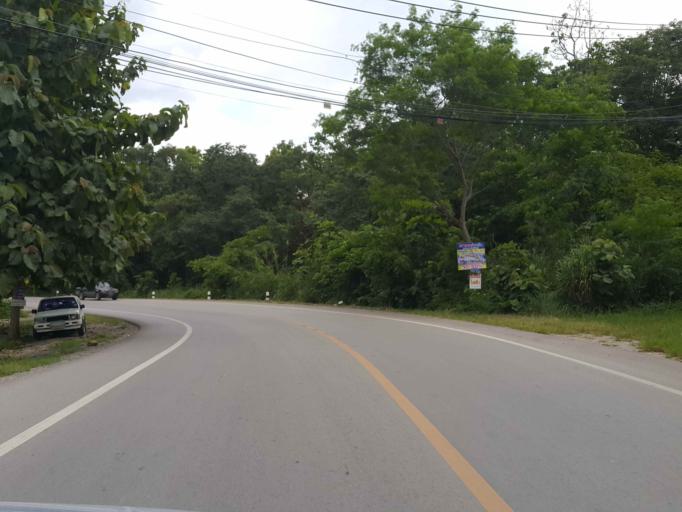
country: TH
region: Chiang Mai
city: San Sai
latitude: 18.9206
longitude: 98.9195
